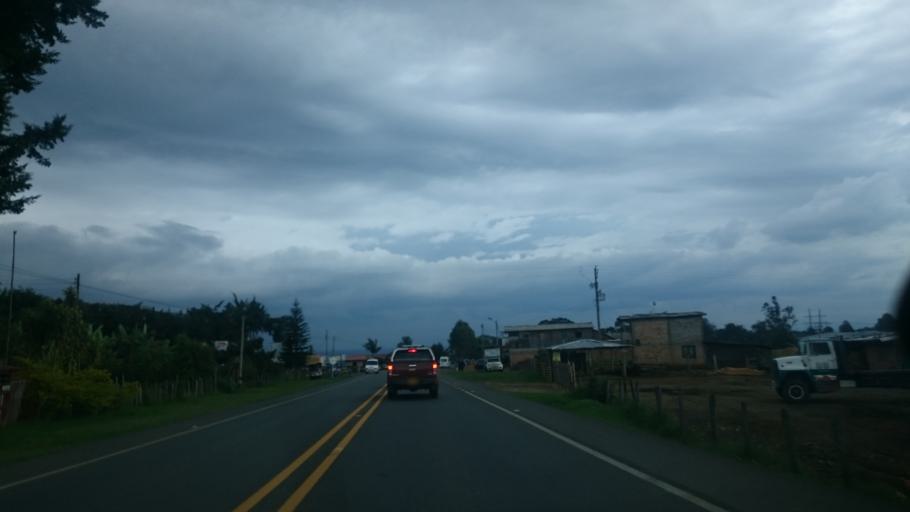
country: CO
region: Cauca
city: Cajibio
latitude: 2.5850
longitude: -76.5391
